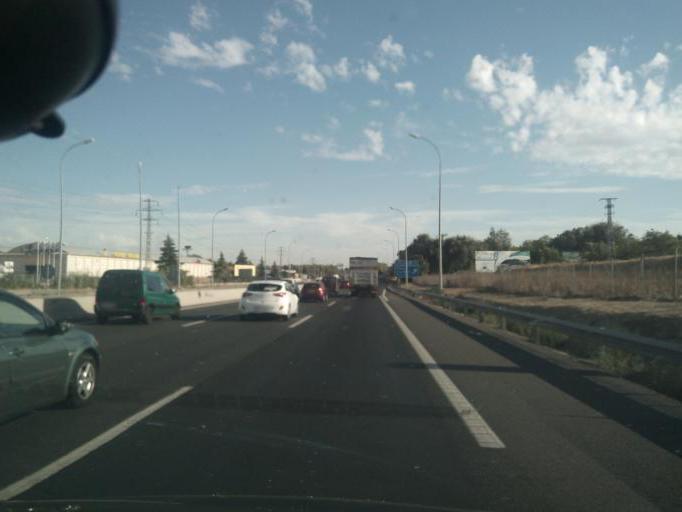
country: ES
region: Madrid
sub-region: Provincia de Madrid
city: Pinto
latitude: 40.2585
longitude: -3.6903
